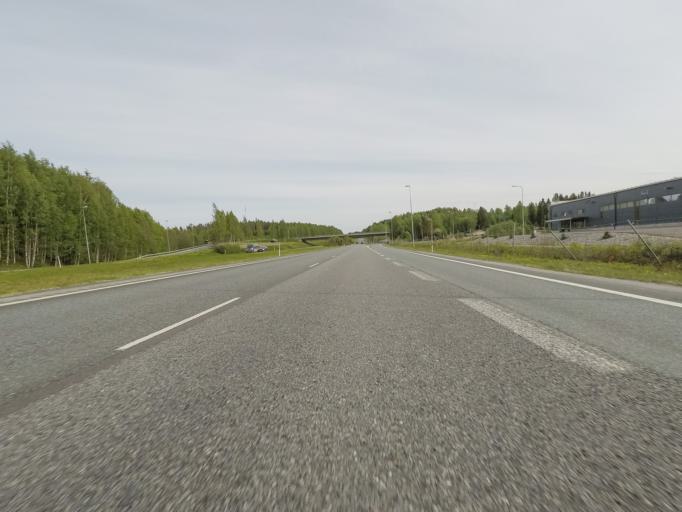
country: FI
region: Haeme
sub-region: Haemeenlinna
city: Parola
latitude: 61.0505
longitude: 24.3556
